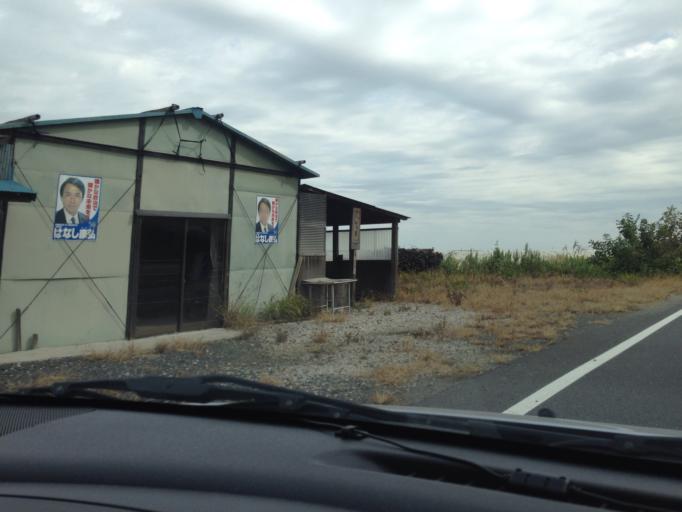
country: JP
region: Ibaraki
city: Ami
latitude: 36.0324
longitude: 140.2566
